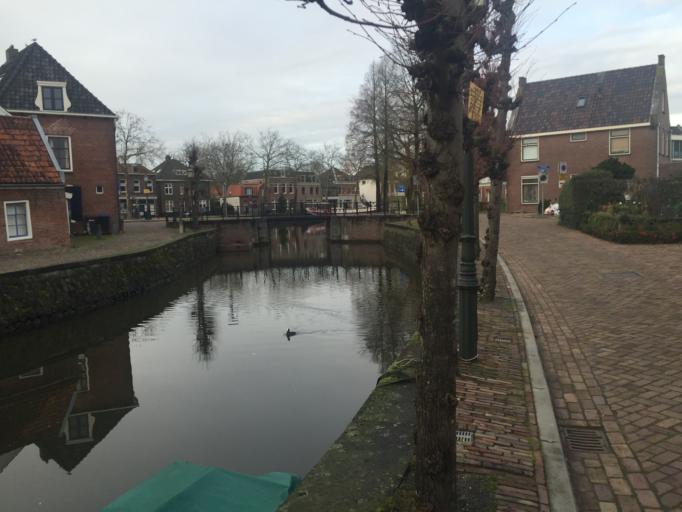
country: NL
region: Utrecht
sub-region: Gemeente Vianen
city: Vianen
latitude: 52.0049
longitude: 5.0967
